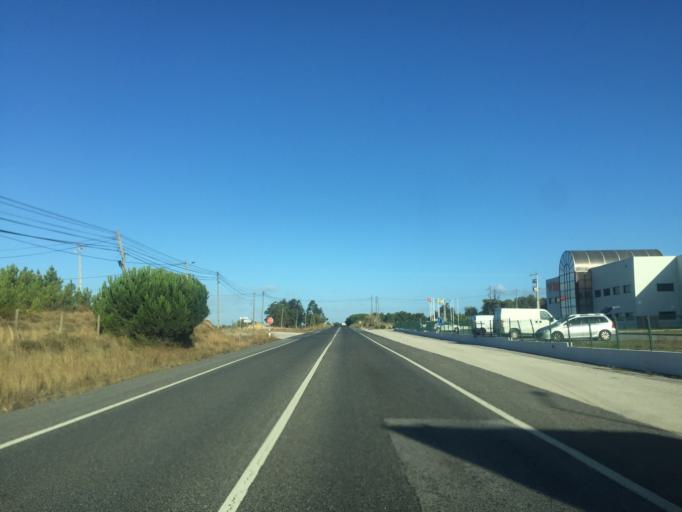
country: PT
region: Lisbon
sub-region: Azambuja
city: Aveiras de Cima
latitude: 39.1648
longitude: -8.9194
